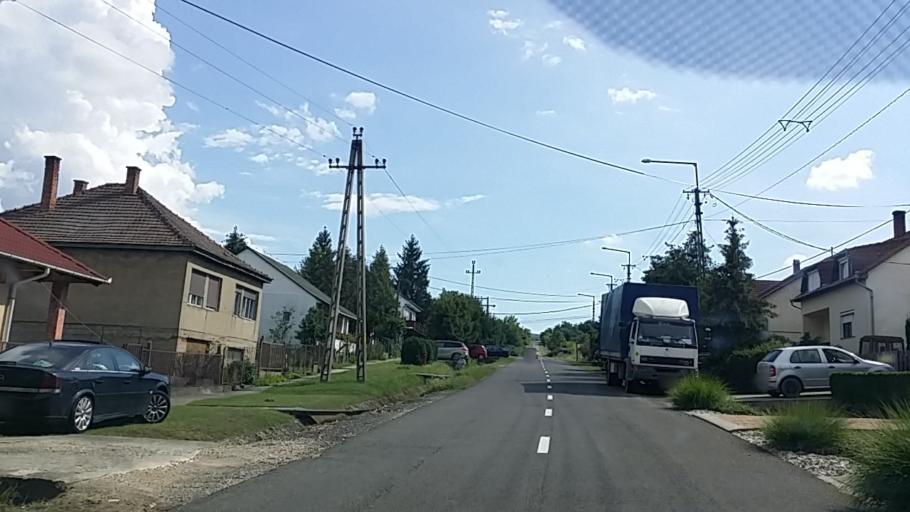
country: HU
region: Nograd
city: Nagyoroszi
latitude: 48.0491
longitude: 19.0446
